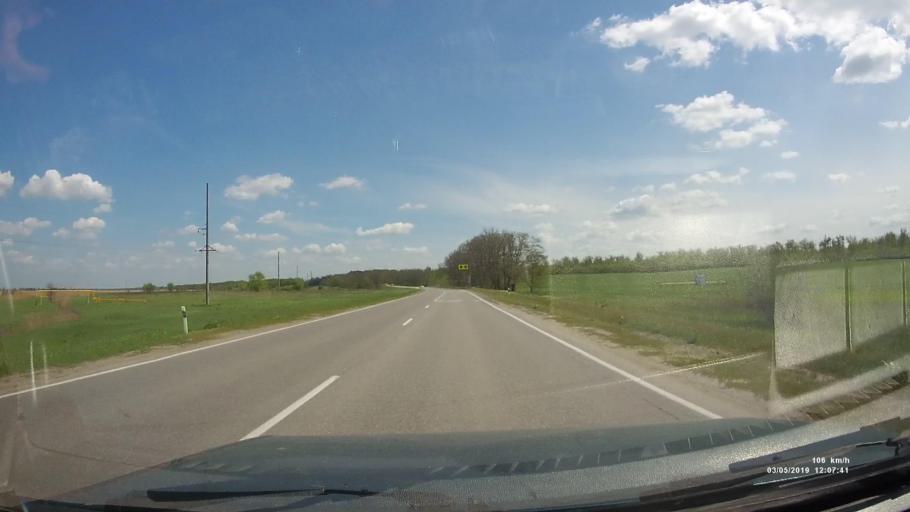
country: RU
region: Rostov
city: Bagayevskaya
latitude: 47.2844
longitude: 40.4809
